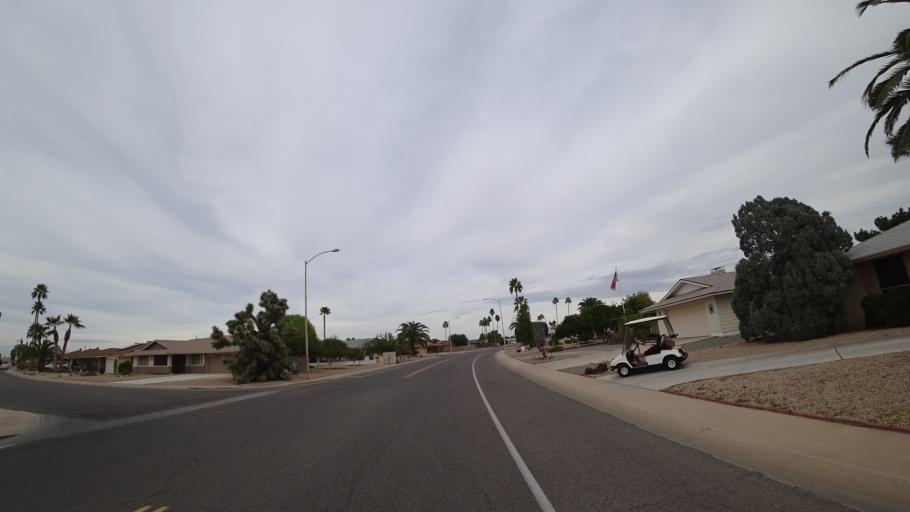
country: US
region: Arizona
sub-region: Maricopa County
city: Youngtown
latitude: 33.6151
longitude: -112.2982
